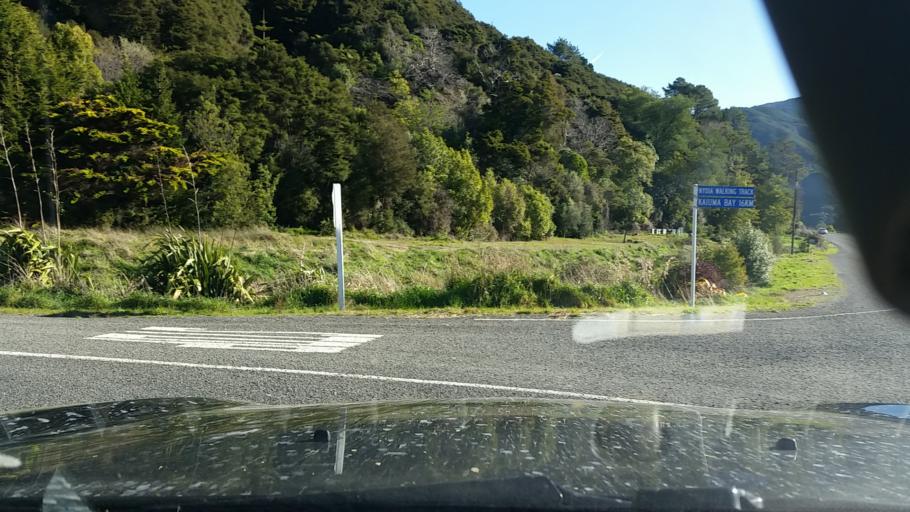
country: NZ
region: Marlborough
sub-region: Marlborough District
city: Picton
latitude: -41.2755
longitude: 173.7380
